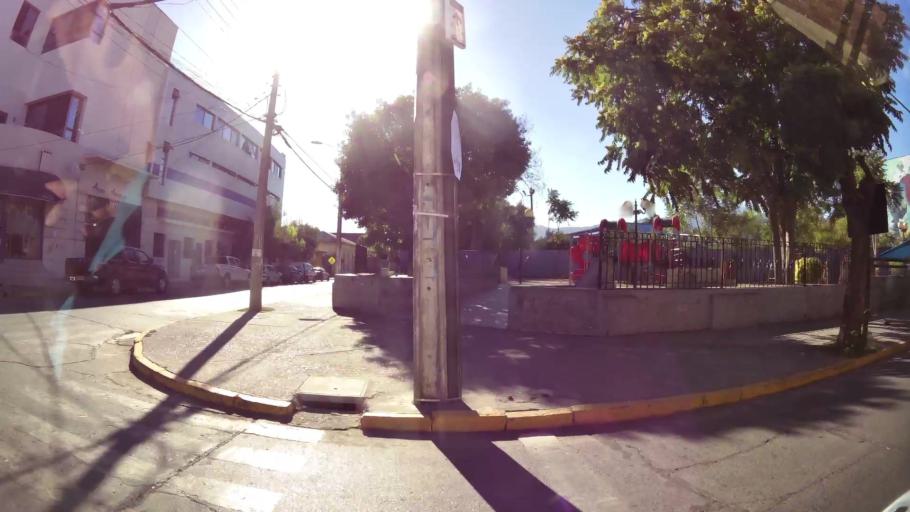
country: CL
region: O'Higgins
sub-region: Provincia de Colchagua
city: Chimbarongo
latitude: -34.5831
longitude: -70.9896
